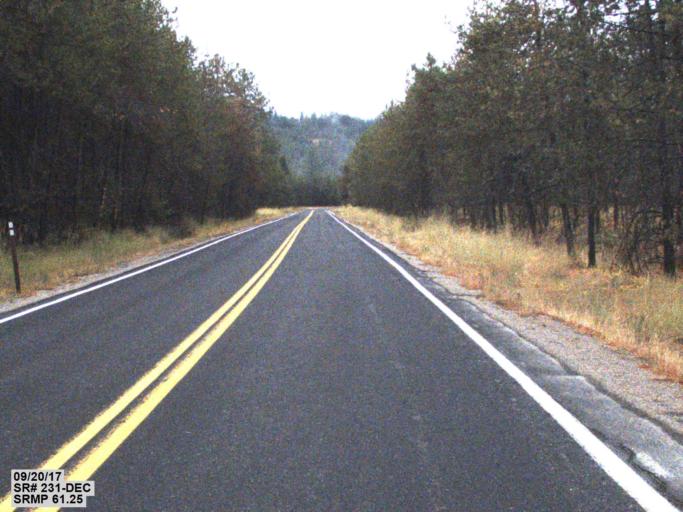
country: US
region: Washington
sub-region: Stevens County
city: Chewelah
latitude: 48.0440
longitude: -117.7404
